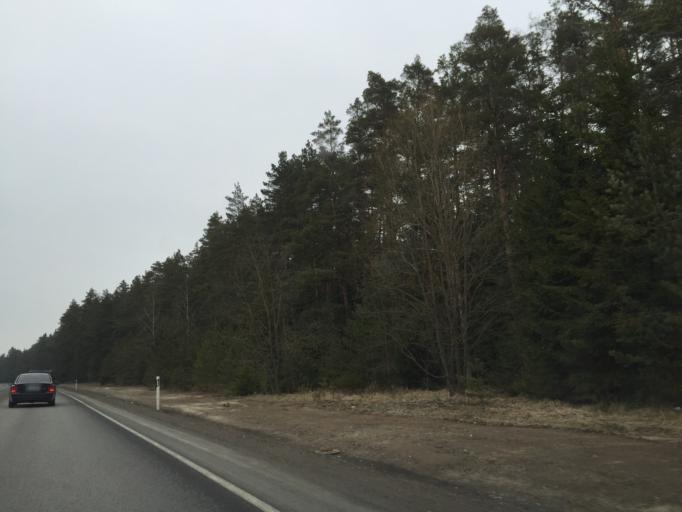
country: EE
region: Paernumaa
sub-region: Paikuse vald
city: Paikuse
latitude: 58.3263
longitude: 24.5974
